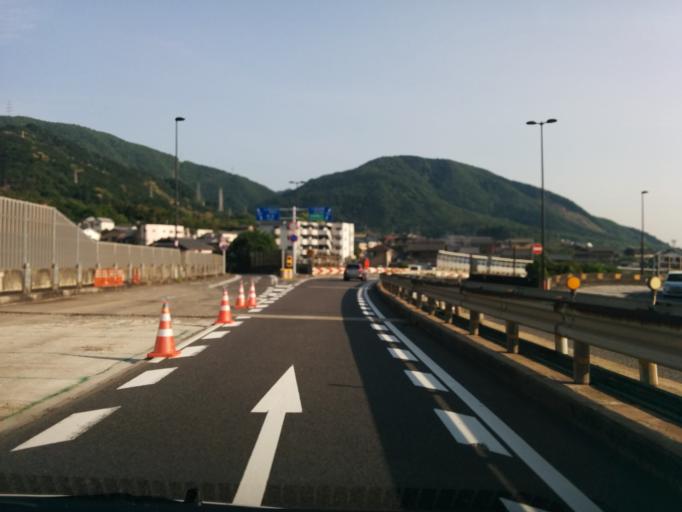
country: JP
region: Shiga Prefecture
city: Otsu-shi
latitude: 34.9929
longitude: 135.8345
